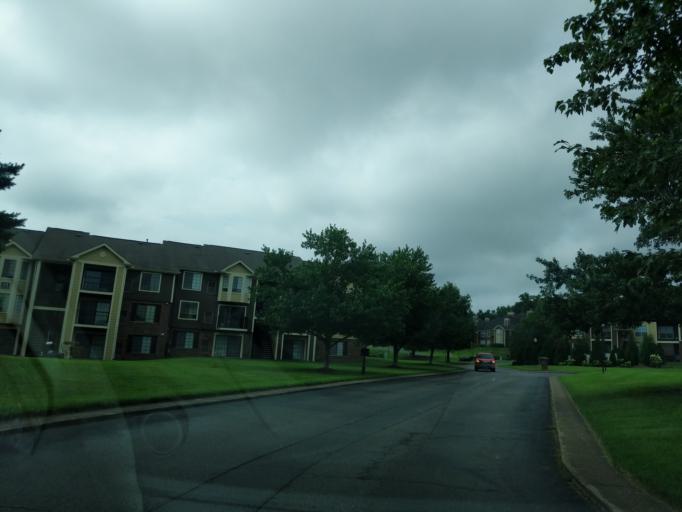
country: US
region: Tennessee
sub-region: Davidson County
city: Lakewood
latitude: 36.1731
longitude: -86.6103
